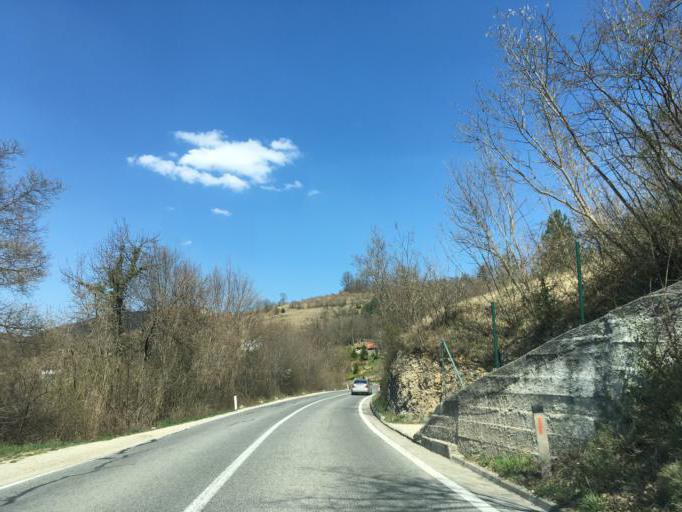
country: BA
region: Federation of Bosnia and Herzegovina
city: Divicani
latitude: 44.3597
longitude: 17.3000
